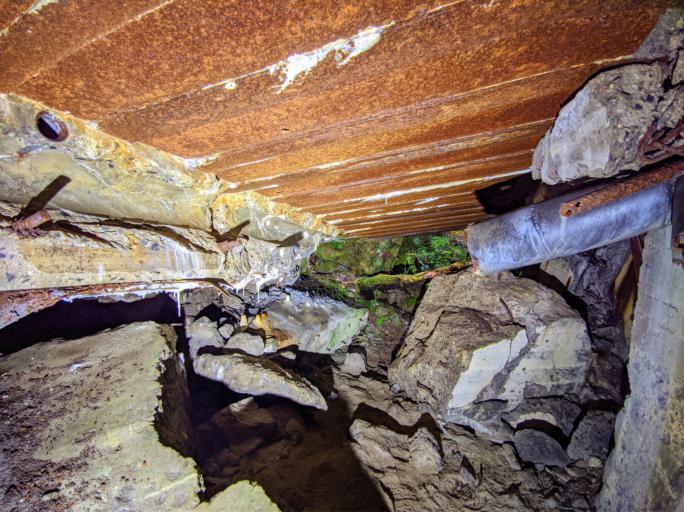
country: PL
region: Lubusz
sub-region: Powiat swiebodzinski
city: Miedzylesie
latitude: 52.0772
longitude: 15.3850
